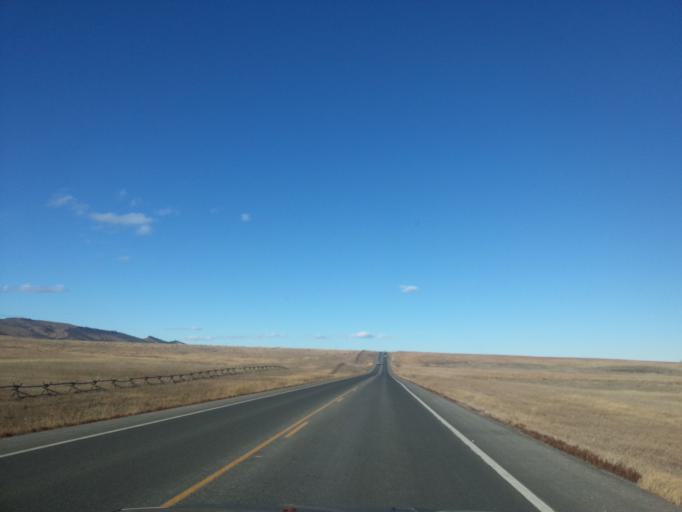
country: US
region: Colorado
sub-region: Larimer County
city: Loveland
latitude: 40.4810
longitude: -105.1156
